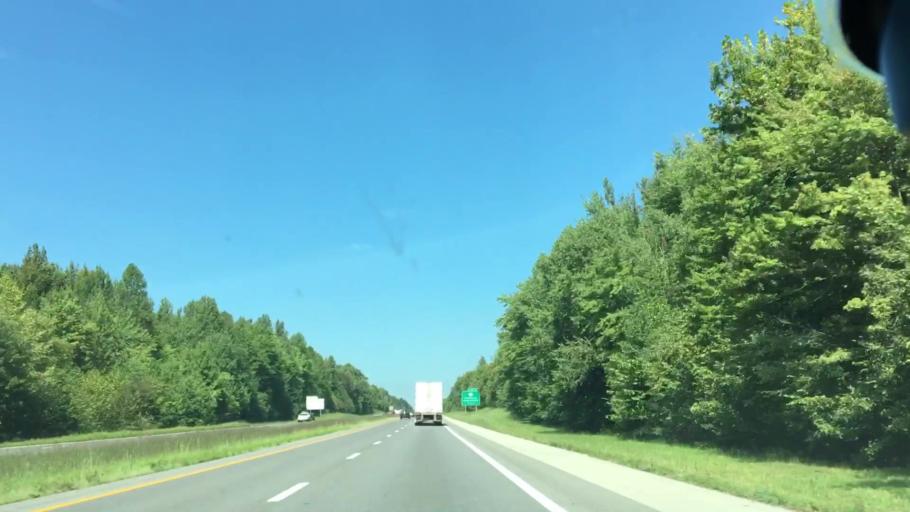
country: US
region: Kentucky
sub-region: Hopkins County
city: Earlington
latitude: 37.2617
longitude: -87.4522
